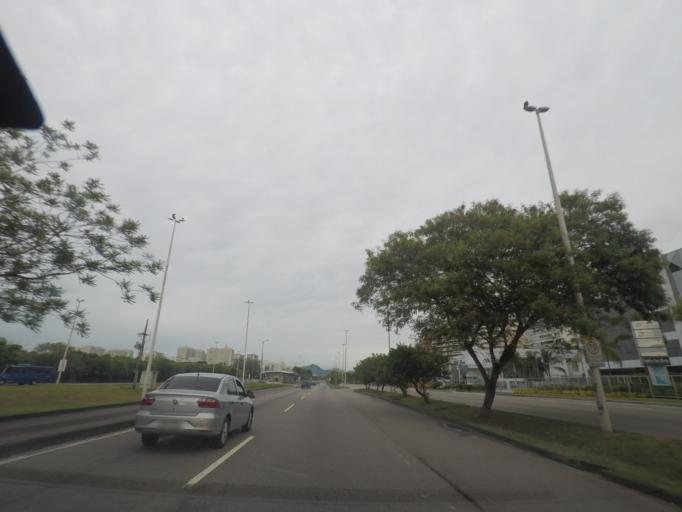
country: BR
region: Rio de Janeiro
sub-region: Nilopolis
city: Nilopolis
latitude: -23.0022
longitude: -43.4224
